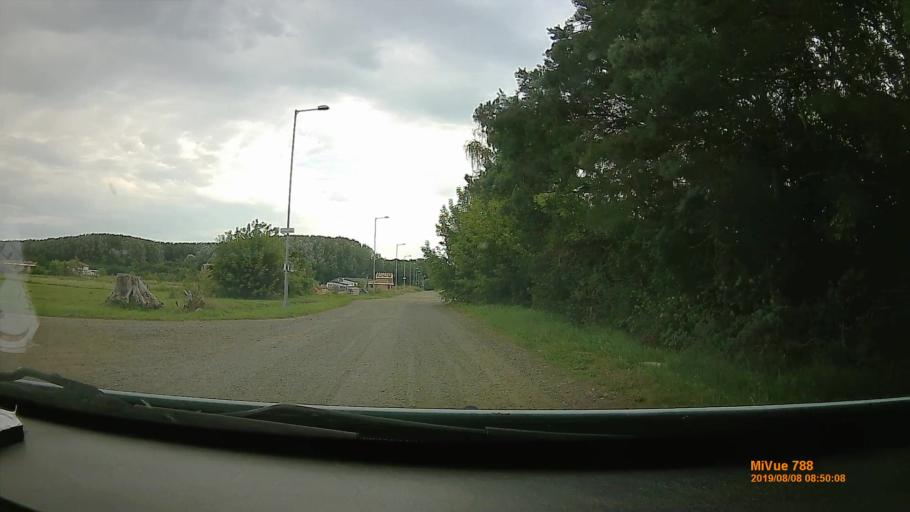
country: HU
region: Hajdu-Bihar
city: Debrecen
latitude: 47.6000
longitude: 21.6443
